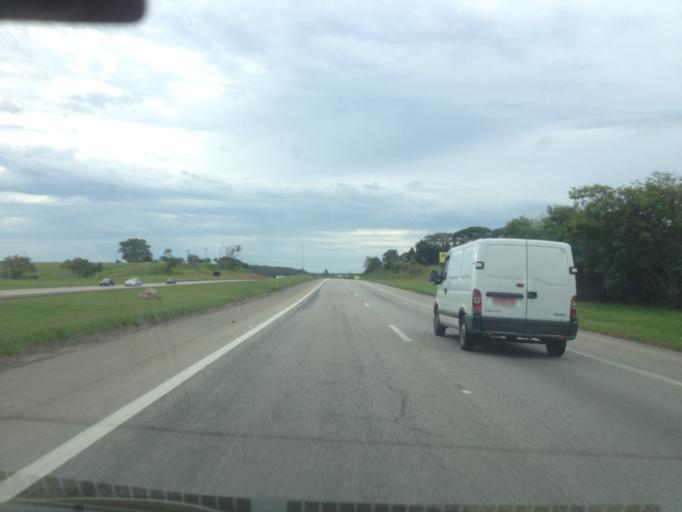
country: BR
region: Sao Paulo
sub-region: Sorocaba
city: Sorocaba
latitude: -23.3856
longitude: -47.3798
